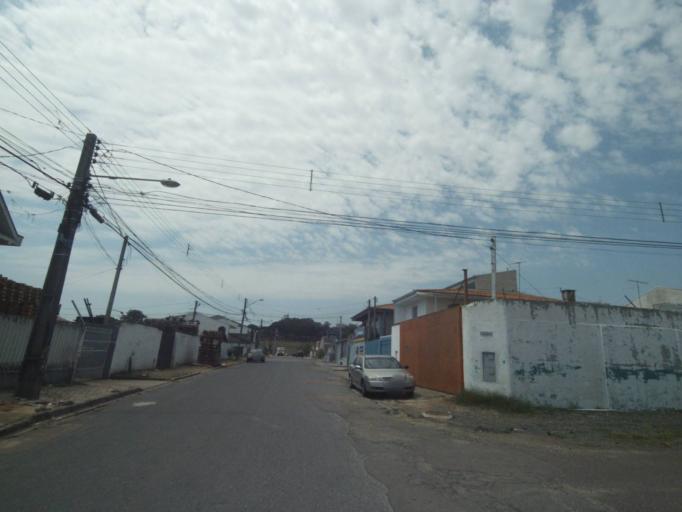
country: BR
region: Parana
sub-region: Sao Jose Dos Pinhais
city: Sao Jose dos Pinhais
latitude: -25.5239
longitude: -49.2630
